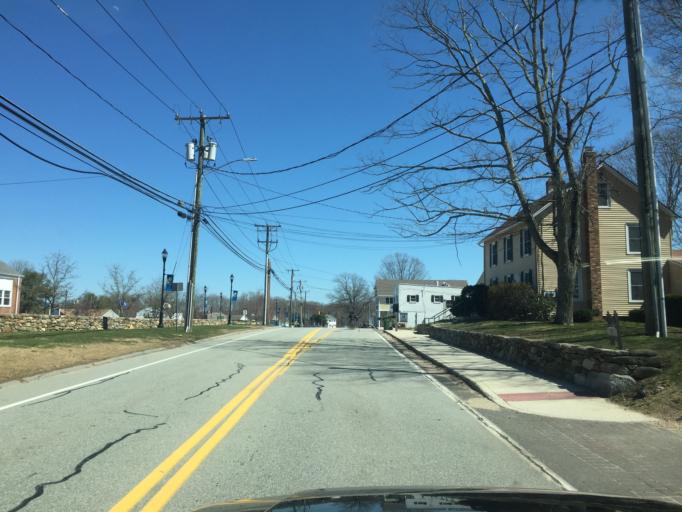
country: US
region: Connecticut
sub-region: Hartford County
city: Terramuggus
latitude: 41.6324
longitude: -72.4625
